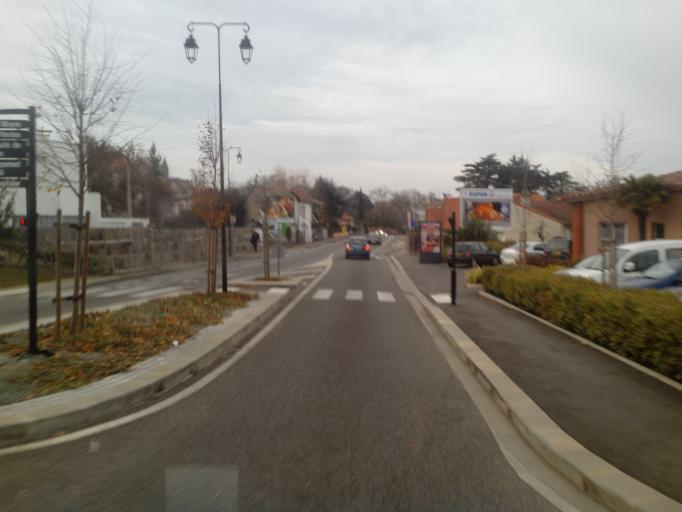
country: FR
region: Midi-Pyrenees
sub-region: Departement de l'Ariege
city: Pamiers
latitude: 43.1112
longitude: 1.6133
